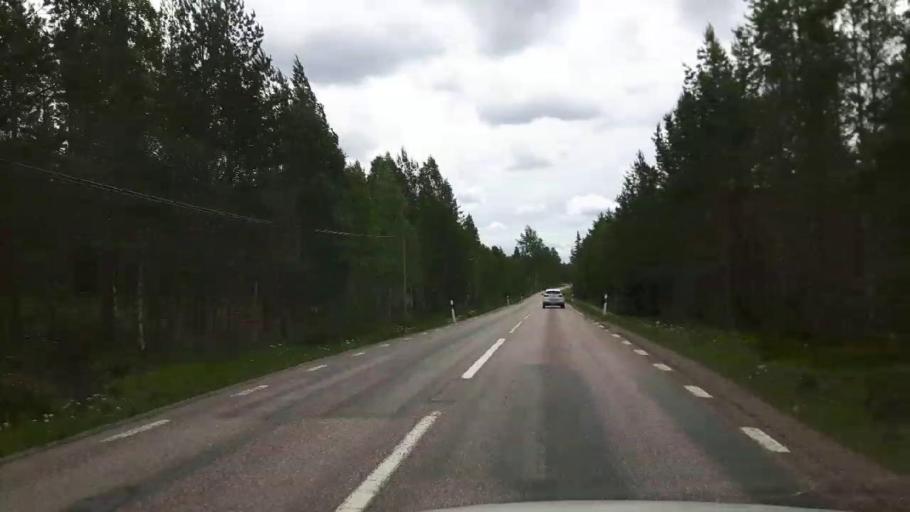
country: SE
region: Vaestmanland
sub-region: Norbergs Kommun
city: Norberg
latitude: 60.1174
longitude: 15.9204
